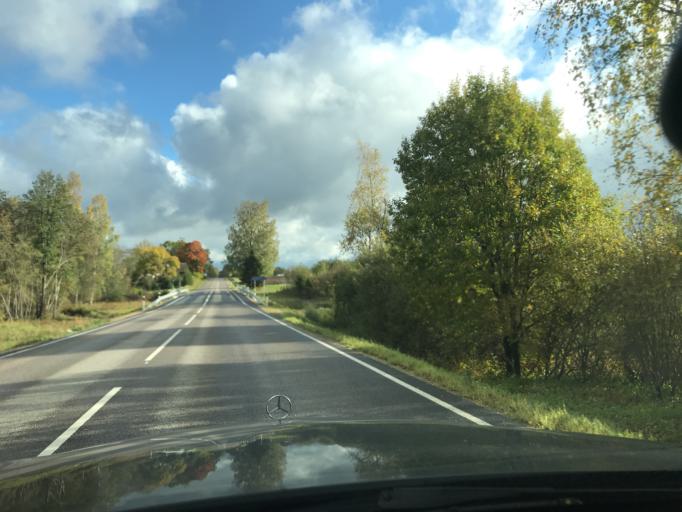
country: EE
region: Valgamaa
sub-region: Torva linn
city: Torva
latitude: 58.0247
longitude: 25.8231
